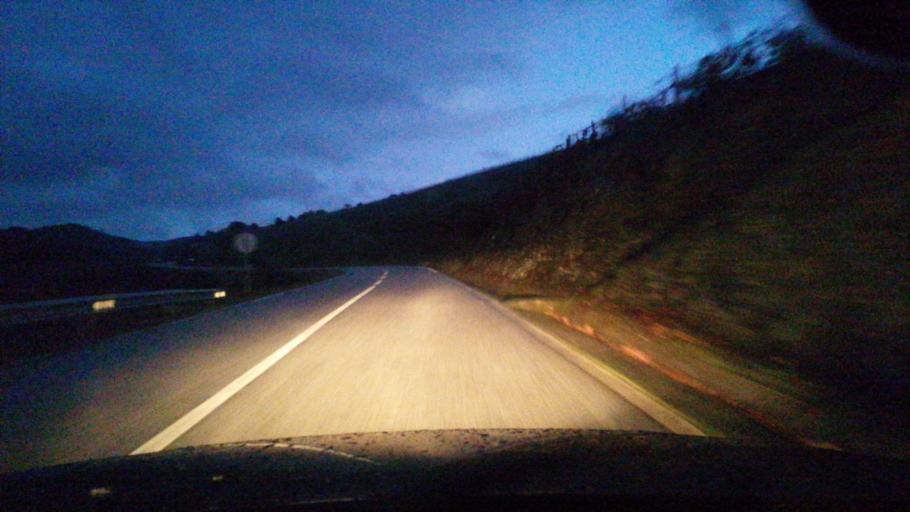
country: PT
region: Viseu
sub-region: Tabuaco
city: Tabuaco
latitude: 41.1472
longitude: -7.5432
